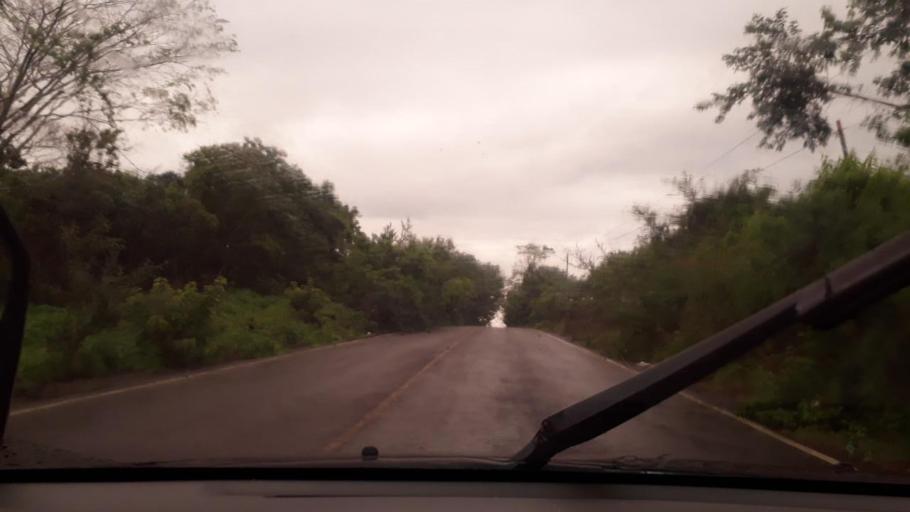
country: GT
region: Jutiapa
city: Comapa
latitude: 14.0466
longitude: -89.9248
